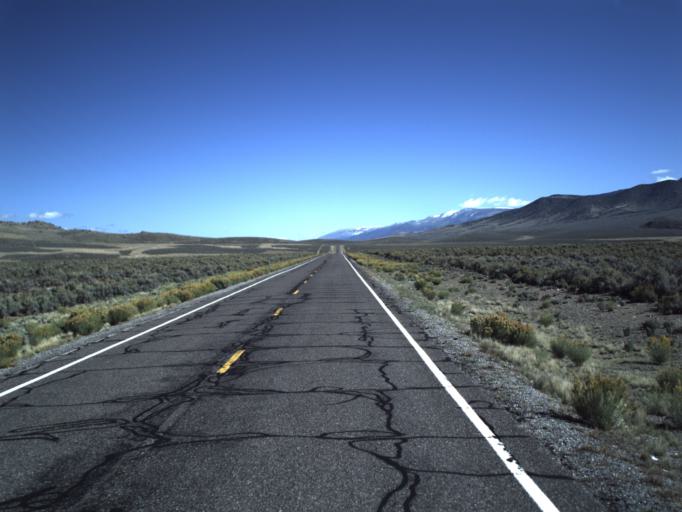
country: US
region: Utah
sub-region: Piute County
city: Junction
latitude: 38.2855
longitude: -111.9794
